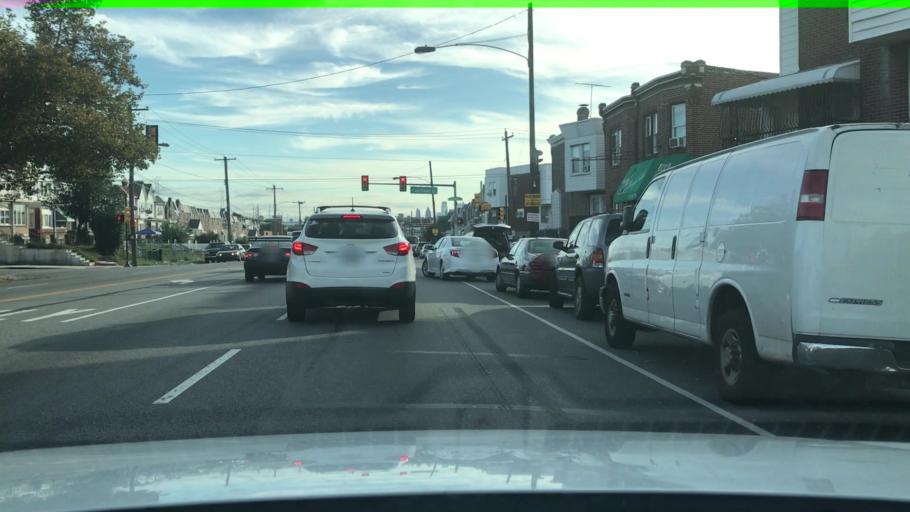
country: US
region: Pennsylvania
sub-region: Montgomery County
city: Rockledge
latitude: 40.0193
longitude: -75.1151
